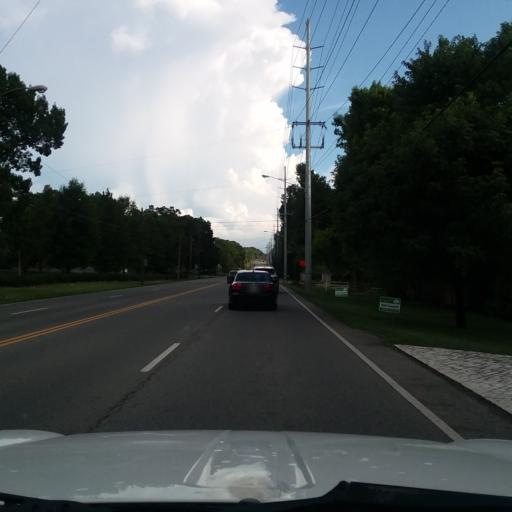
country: US
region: Tennessee
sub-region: Davidson County
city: Oak Hill
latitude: 36.0849
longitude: -86.7723
